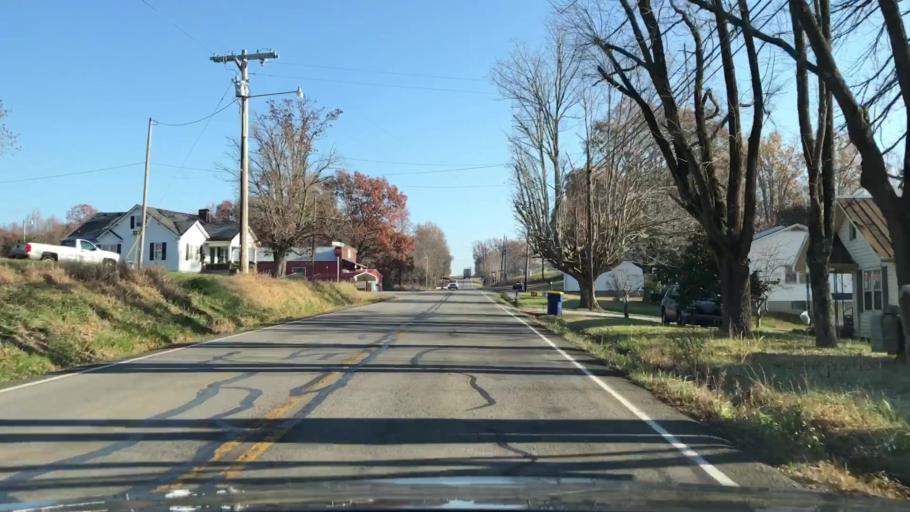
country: US
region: Kentucky
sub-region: Edmonson County
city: Brownsville
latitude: 37.2386
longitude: -86.2905
